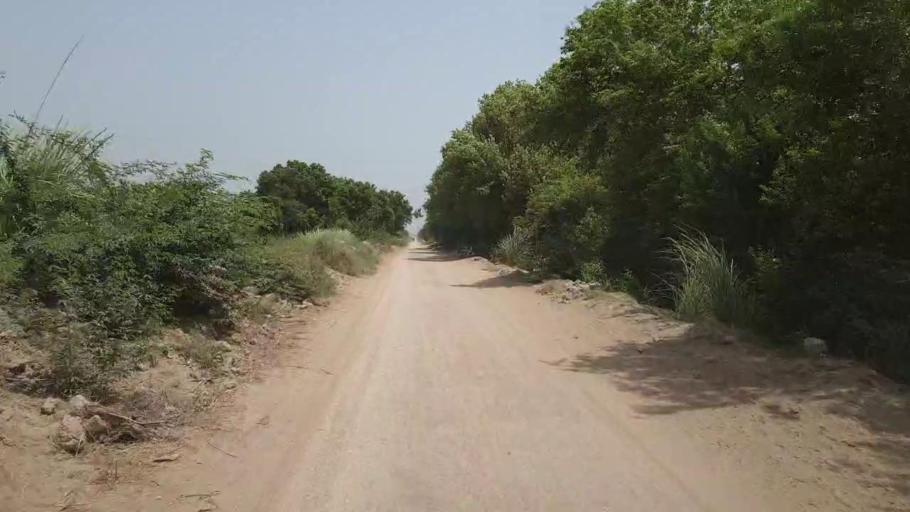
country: PK
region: Sindh
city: Nawabshah
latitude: 26.3148
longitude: 68.3000
